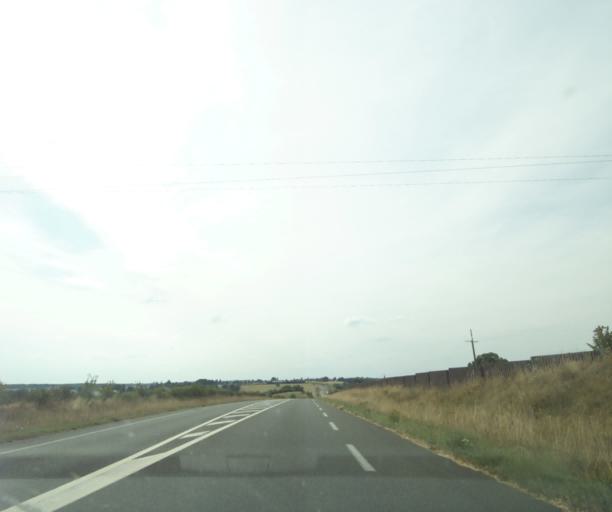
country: FR
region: Pays de la Loire
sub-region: Departement de la Sarthe
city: Chateau-du-Loir
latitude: 47.7043
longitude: 0.4218
